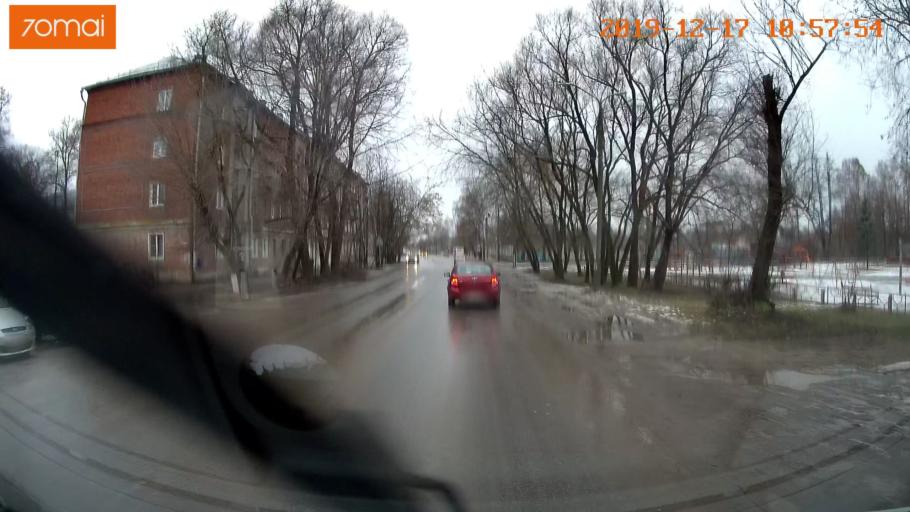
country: RU
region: Vladimir
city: Gus'-Khrustal'nyy
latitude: 55.6219
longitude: 40.6556
